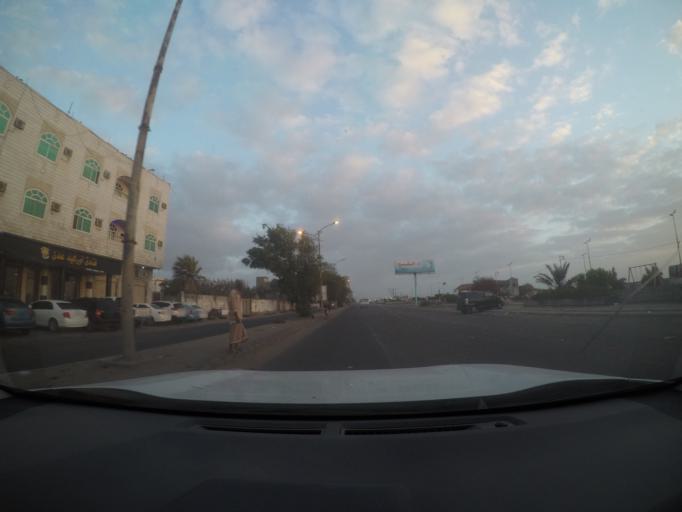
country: YE
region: Aden
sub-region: Khur Maksar
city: Khawr Maksar
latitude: 12.8653
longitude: 45.0617
